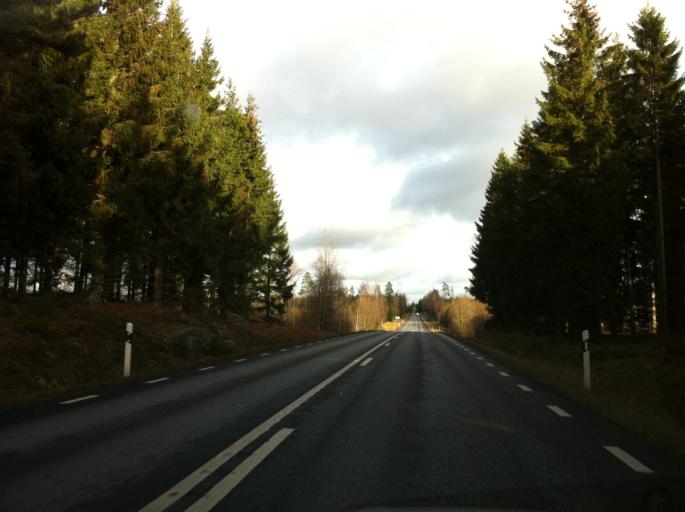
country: SE
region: Kronoberg
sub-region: Alvesta Kommun
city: Vislanda
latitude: 56.7409
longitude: 14.5078
